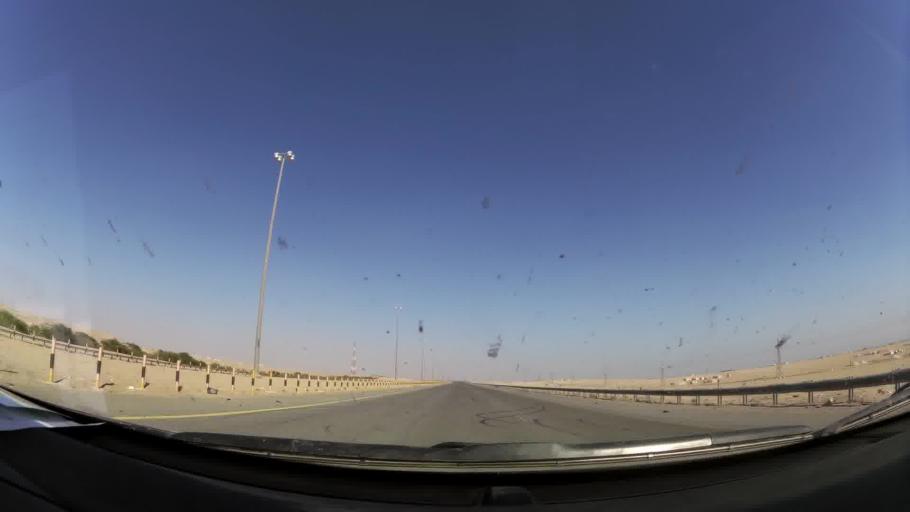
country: KW
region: Muhafazat al Jahra'
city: Al Jahra'
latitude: 29.4444
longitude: 47.7492
